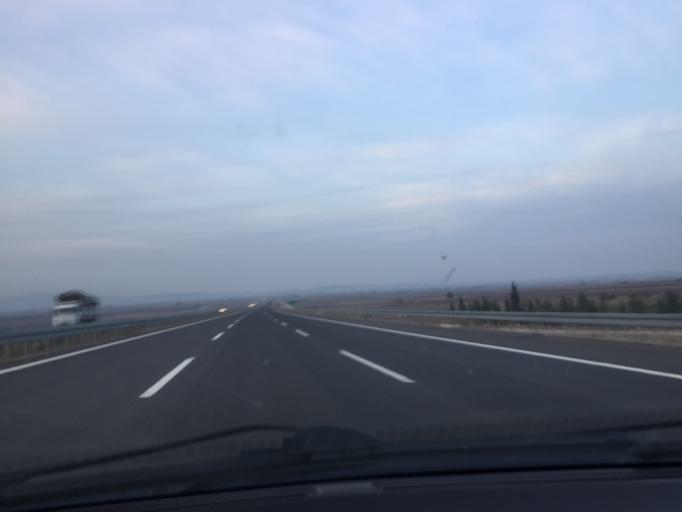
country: TR
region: Manisa
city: Halitpasa
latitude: 38.7041
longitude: 27.6446
